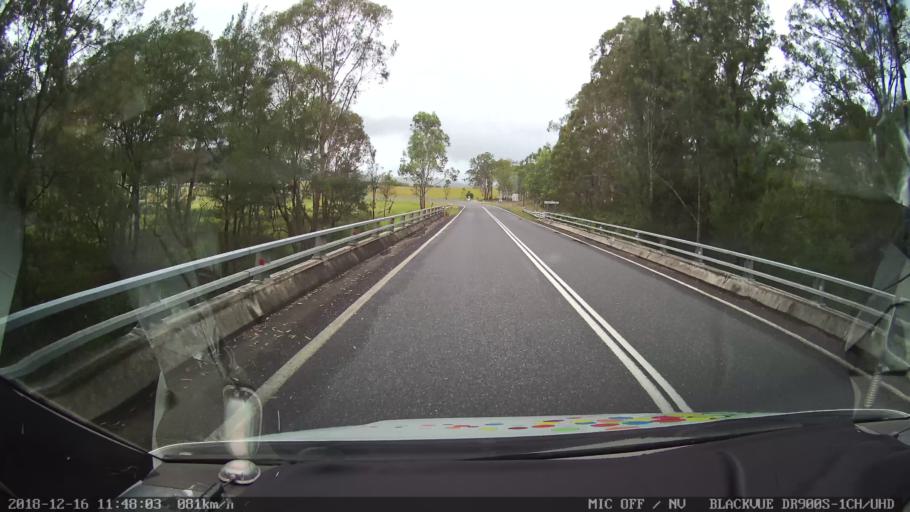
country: AU
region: New South Wales
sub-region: Tenterfield Municipality
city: Carrolls Creek
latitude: -28.9215
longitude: 152.2441
